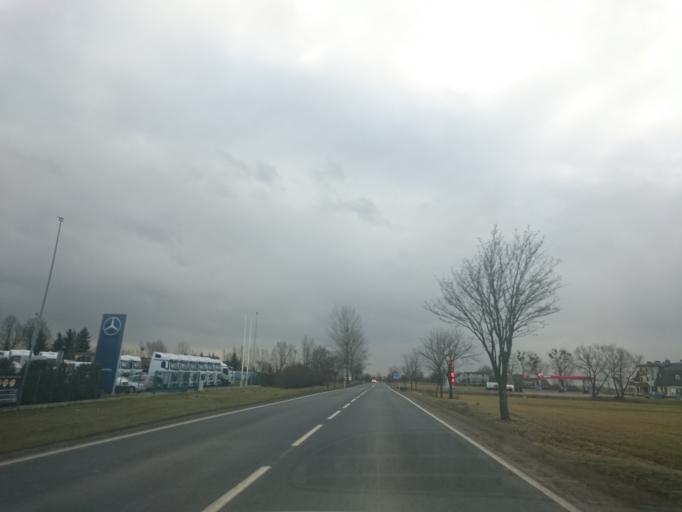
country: PL
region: Kujawsko-Pomorskie
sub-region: Powiat torunski
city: Lubicz Dolny
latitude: 53.0801
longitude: 18.7663
